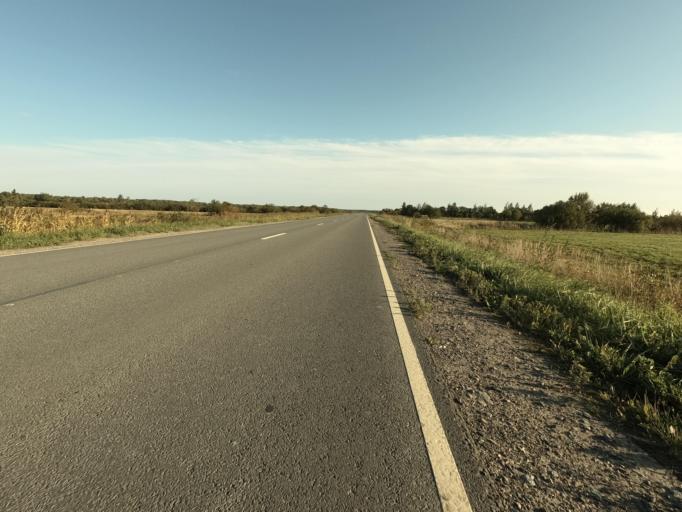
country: RU
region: St.-Petersburg
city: Sapernyy
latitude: 59.7479
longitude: 30.6415
